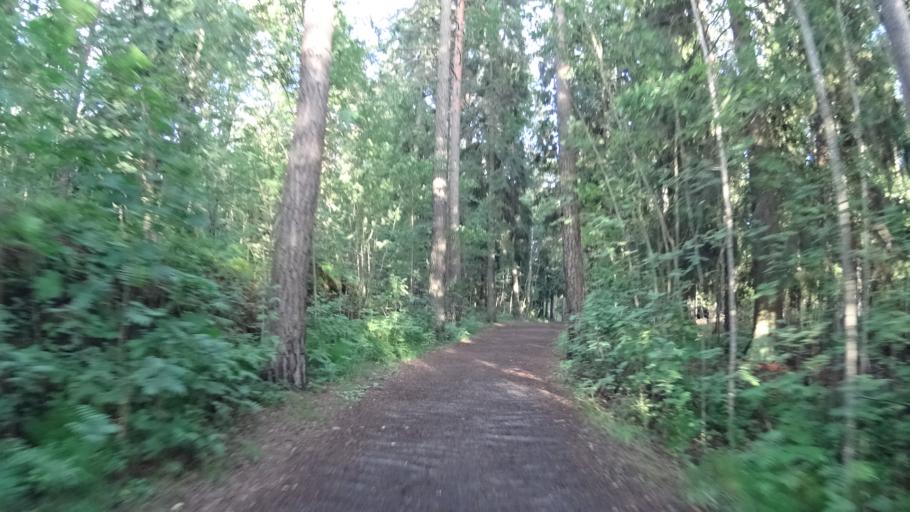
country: FI
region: Uusimaa
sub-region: Helsinki
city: Helsinki
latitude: 60.1910
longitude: 24.8938
